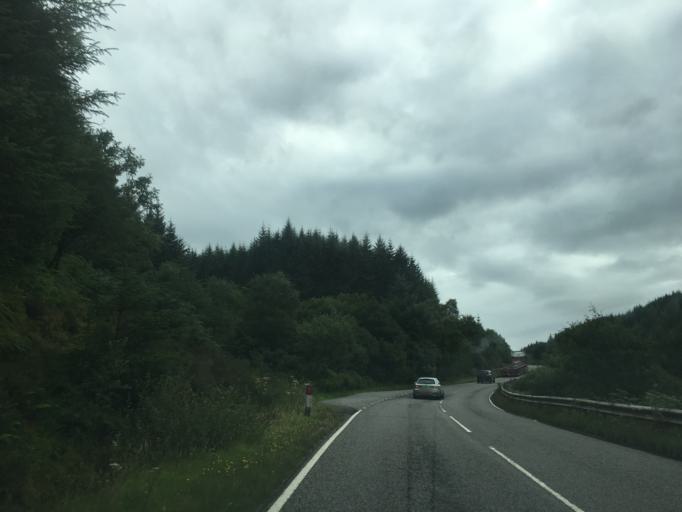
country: GB
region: Scotland
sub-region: Argyll and Bute
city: Oban
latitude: 56.2854
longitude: -5.4767
